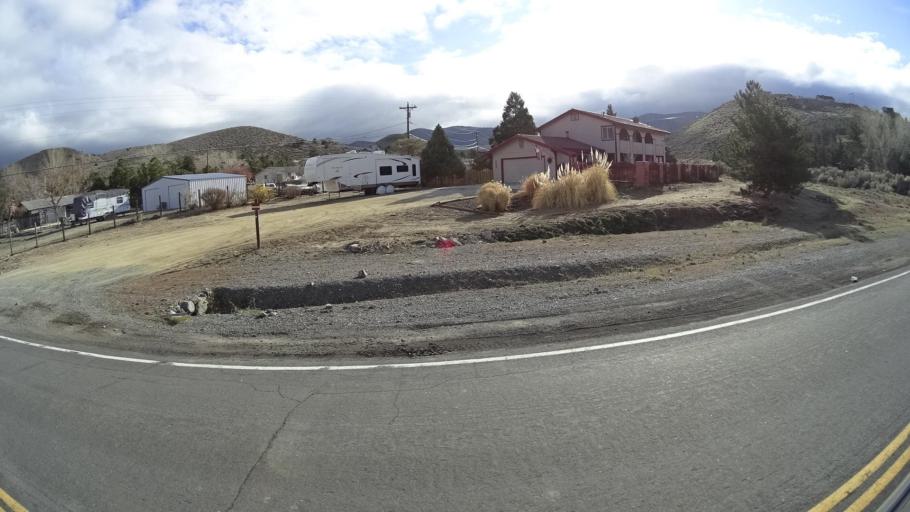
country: US
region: Nevada
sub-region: Storey County
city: Virginia City
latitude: 39.2852
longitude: -119.7594
